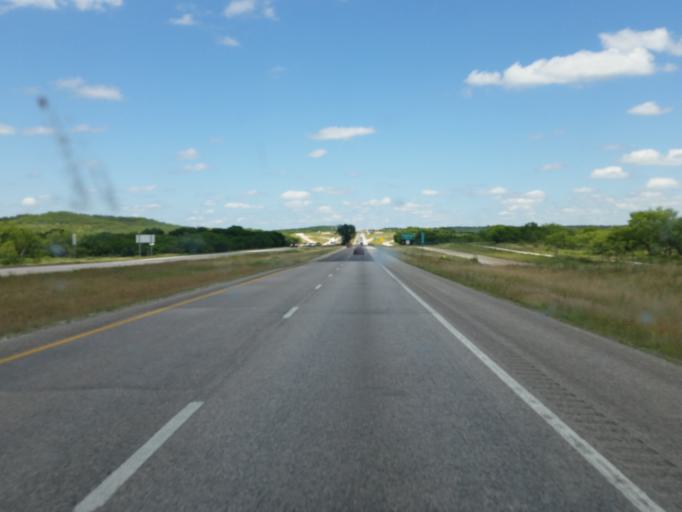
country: US
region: Texas
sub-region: Eastland County
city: Cisco
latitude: 32.3775
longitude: -99.1158
